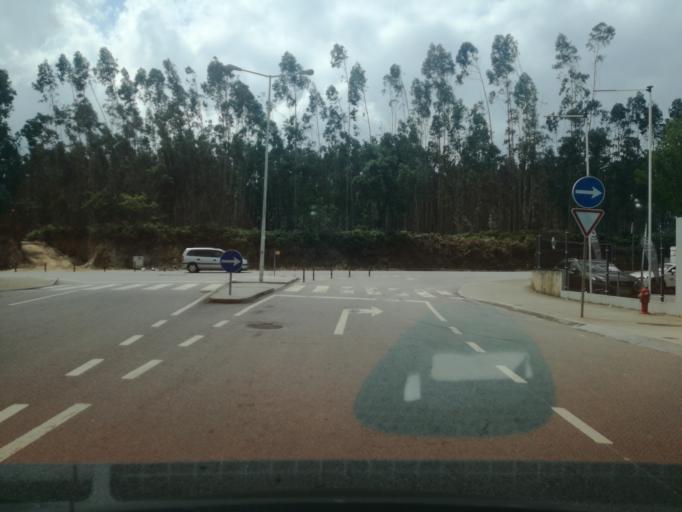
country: PT
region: Porto
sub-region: Maia
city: Anta
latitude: 41.2571
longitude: -8.6319
